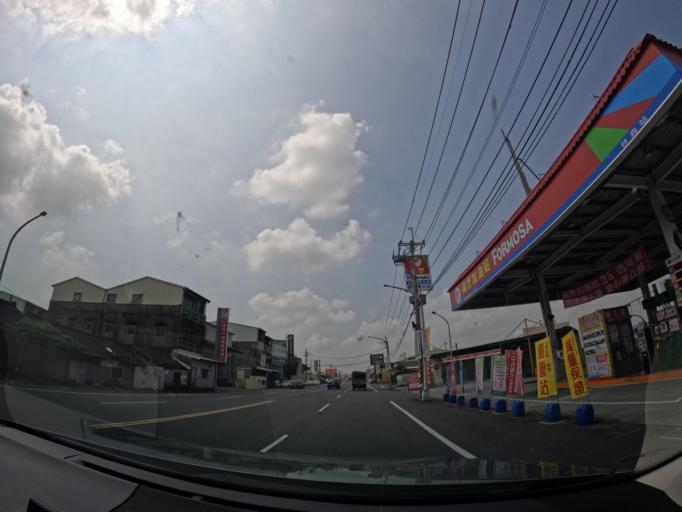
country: TW
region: Taiwan
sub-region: Yunlin
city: Douliu
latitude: 23.6952
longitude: 120.4210
